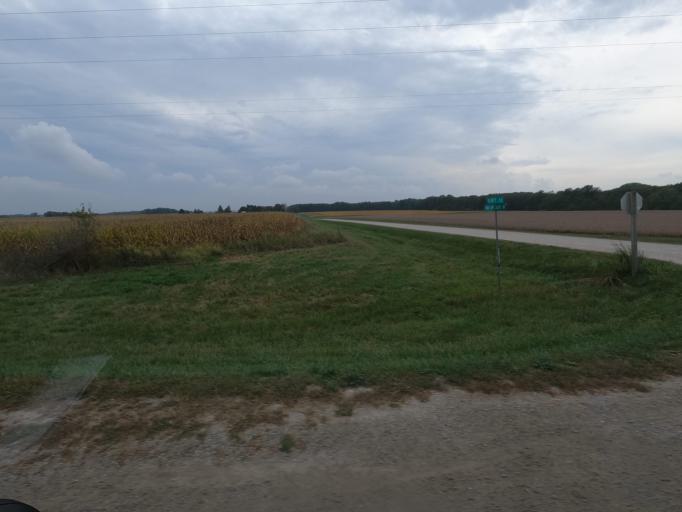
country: US
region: Iowa
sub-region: Van Buren County
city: Keosauqua
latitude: 40.8441
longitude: -92.0252
